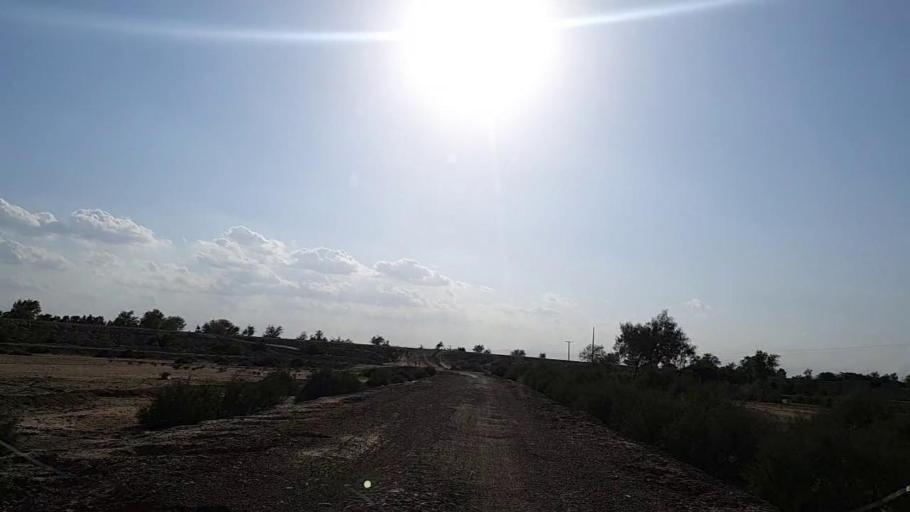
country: PK
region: Sindh
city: Johi
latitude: 26.5857
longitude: 67.5430
